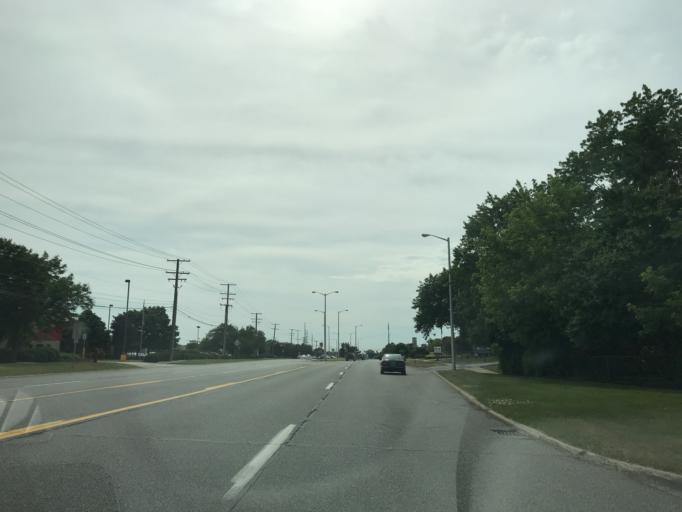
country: US
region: Michigan
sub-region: Oakland County
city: Farmington
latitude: 42.4110
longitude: -83.4086
